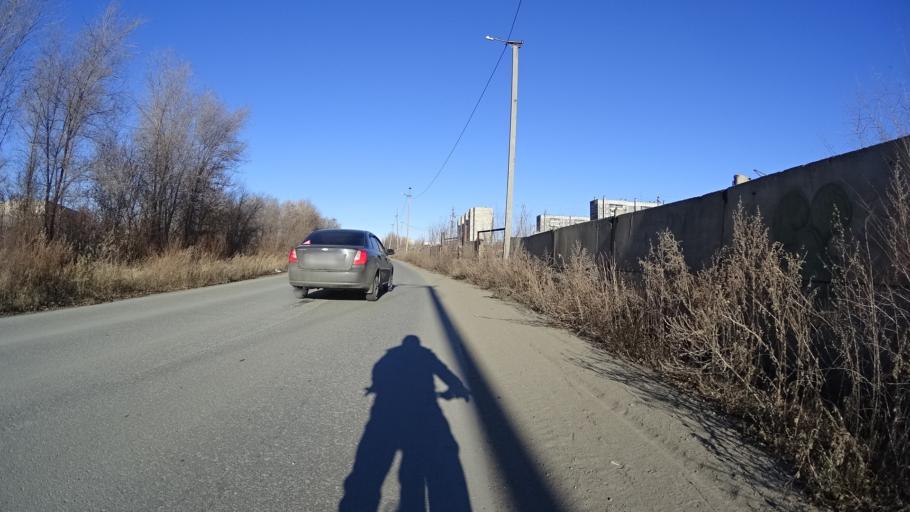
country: RU
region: Chelyabinsk
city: Troitsk
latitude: 54.0443
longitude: 61.6404
